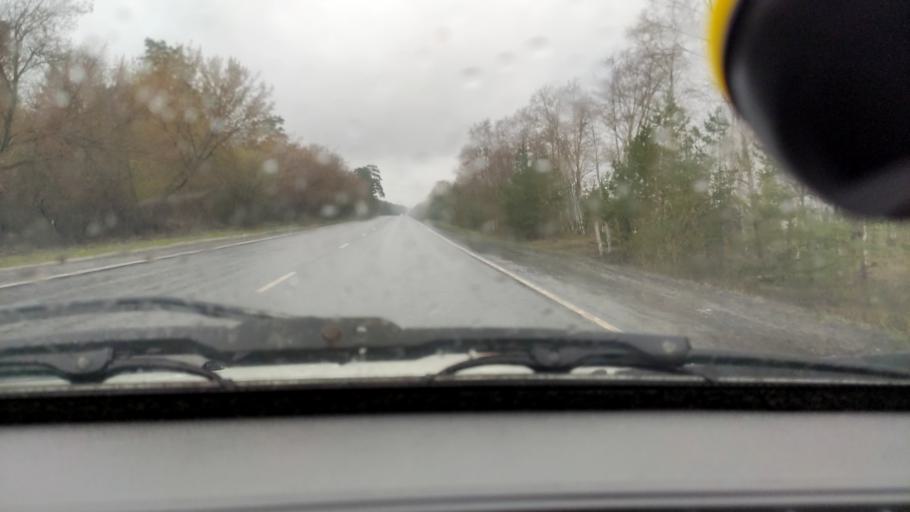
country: RU
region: Samara
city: Povolzhskiy
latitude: 53.6214
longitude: 49.6418
